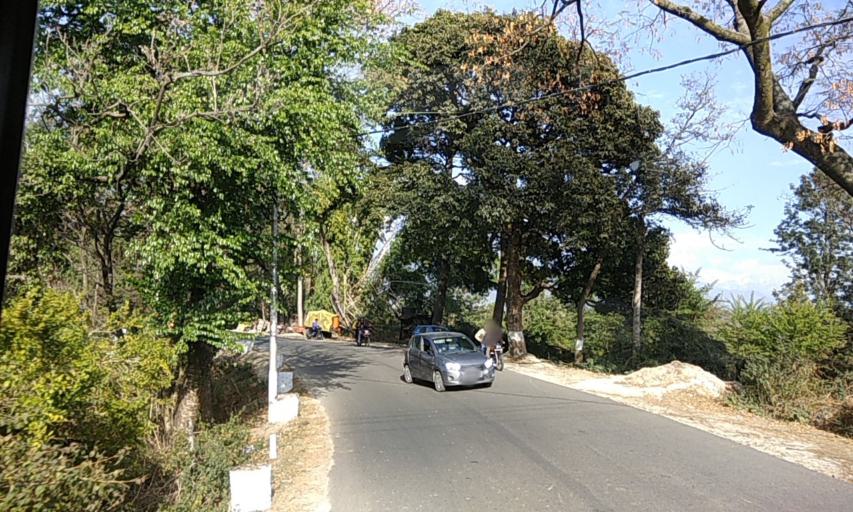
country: IN
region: Himachal Pradesh
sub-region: Kangra
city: Palampur
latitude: 32.0936
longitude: 76.5292
